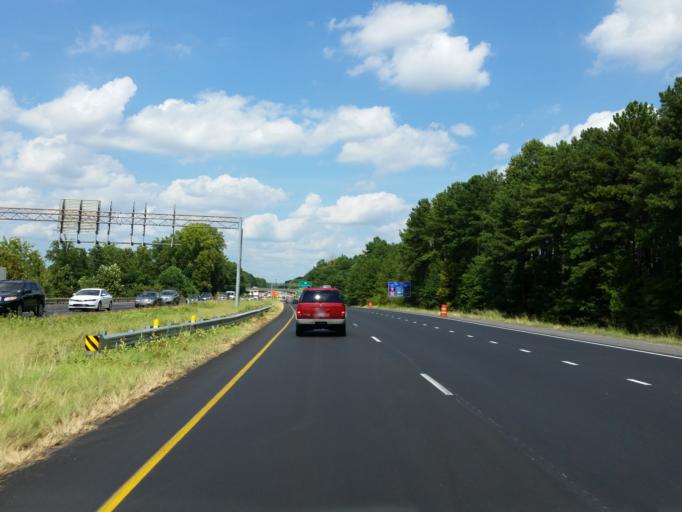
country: US
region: Georgia
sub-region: Gwinnett County
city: Lawrenceville
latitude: 33.9639
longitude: -84.0220
